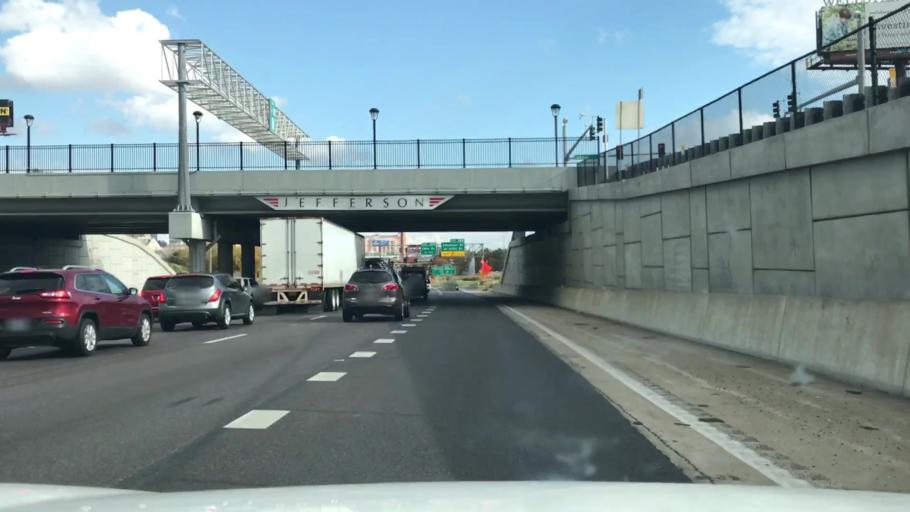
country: US
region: Missouri
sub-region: City of Saint Louis
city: St. Louis
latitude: 38.6275
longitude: -90.2184
